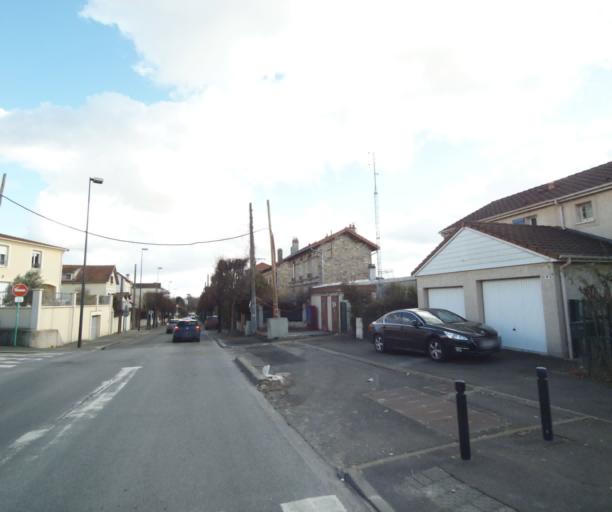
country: FR
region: Ile-de-France
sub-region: Departement de Seine-Saint-Denis
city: Pierrefitte-sur-Seine
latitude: 48.9636
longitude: 2.3540
